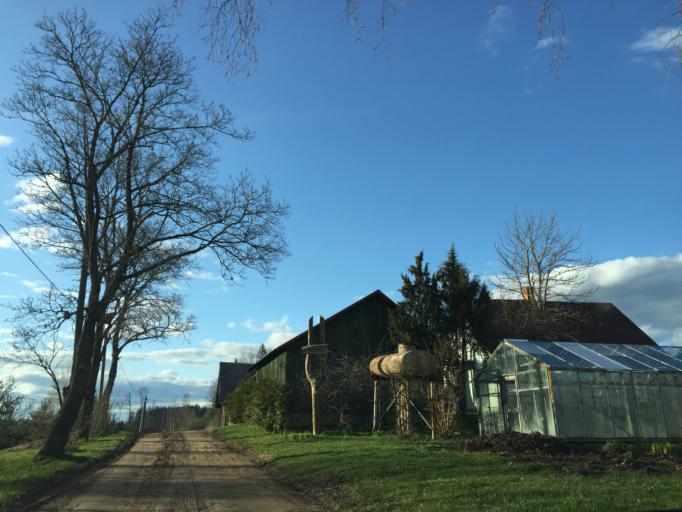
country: LV
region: Rezekne
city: Rezekne
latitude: 56.5782
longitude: 27.3592
